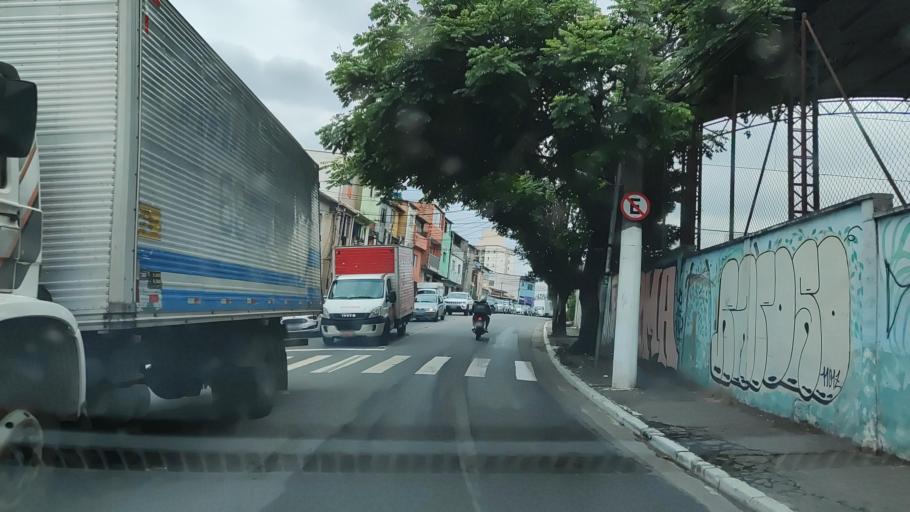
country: BR
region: Sao Paulo
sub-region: Sao Paulo
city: Sao Paulo
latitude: -23.4737
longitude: -46.6498
